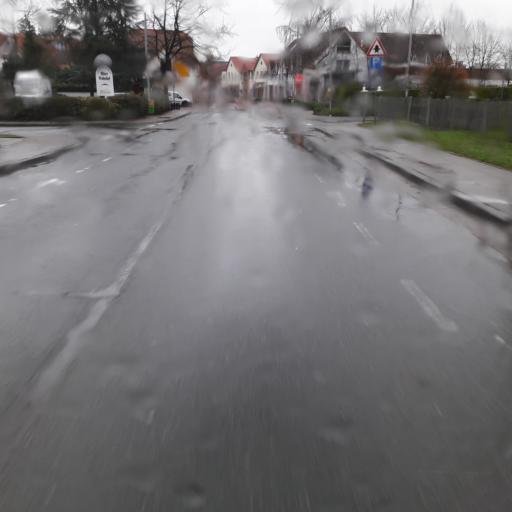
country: DE
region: North Rhine-Westphalia
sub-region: Regierungsbezirk Detmold
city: Petershagen
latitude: 52.3774
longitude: 8.9637
